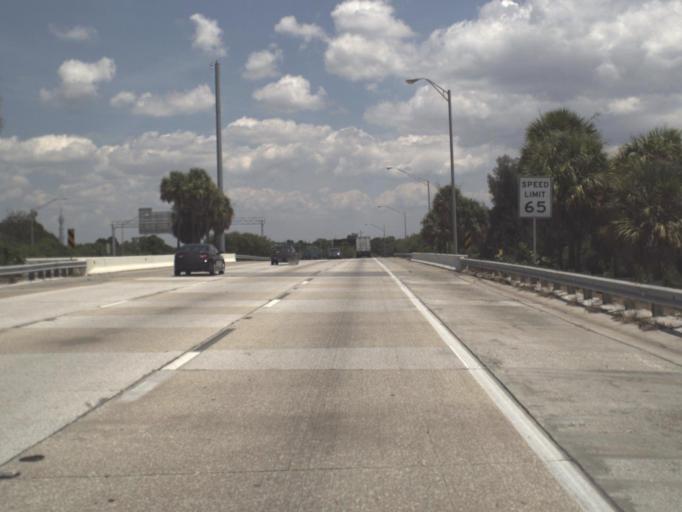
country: US
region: Florida
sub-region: Pinellas County
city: Gulfport
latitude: 27.7331
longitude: -82.6763
